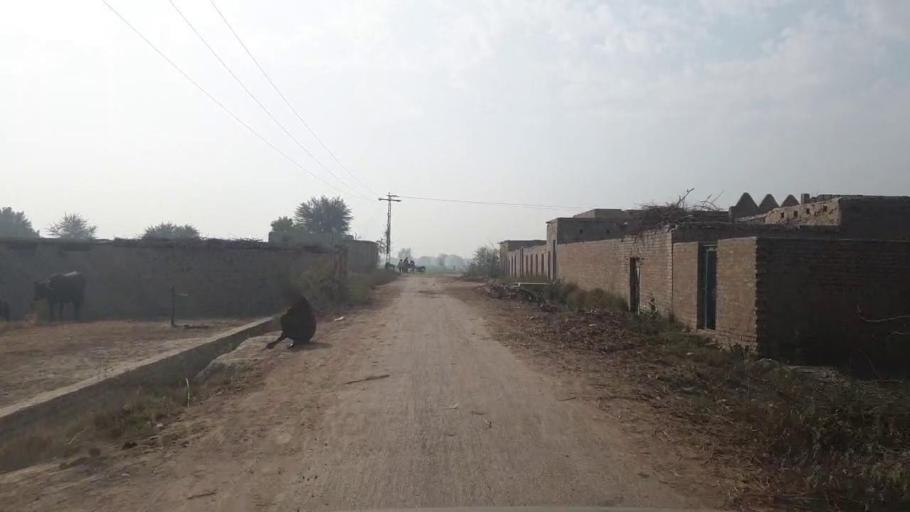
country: PK
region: Sindh
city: Hala
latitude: 25.9053
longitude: 68.4303
